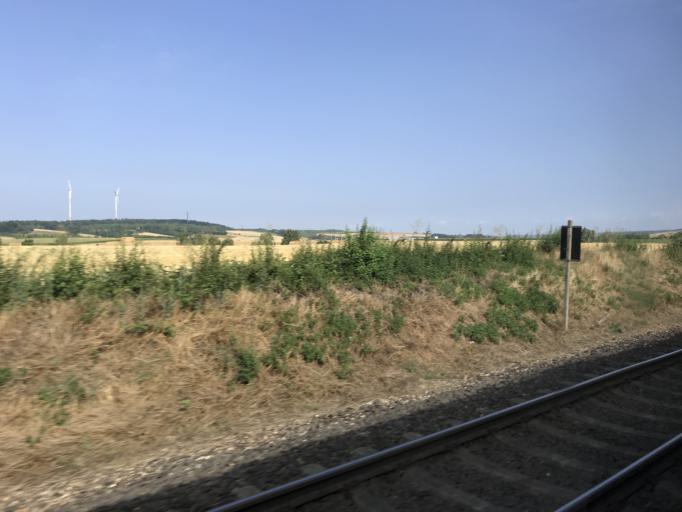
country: DE
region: Hesse
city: Bad Camberg
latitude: 50.2791
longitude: 8.2645
